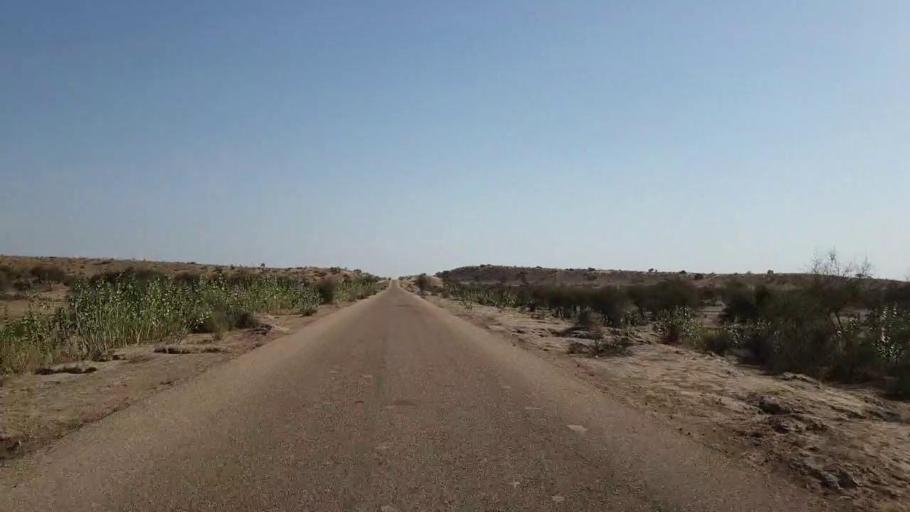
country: PK
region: Sindh
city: Nabisar
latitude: 25.0851
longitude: 70.0414
